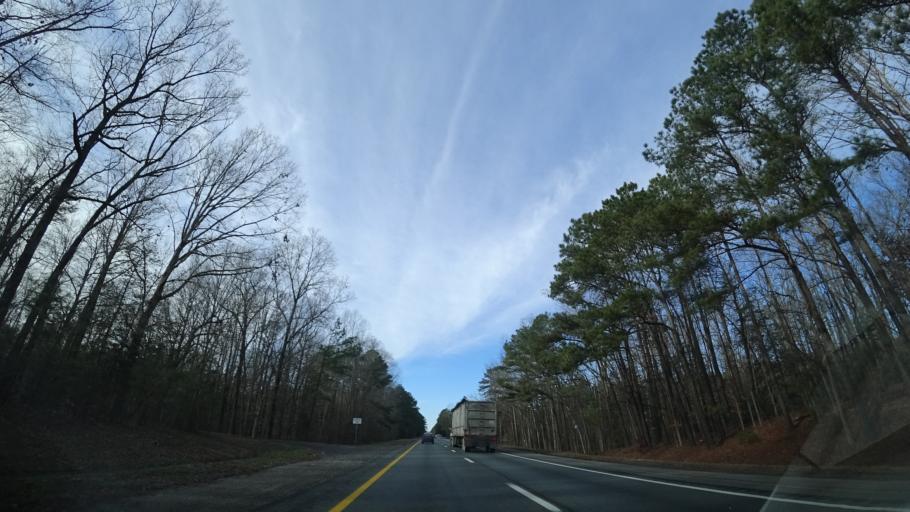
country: US
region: Virginia
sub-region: New Kent County
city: New Kent
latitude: 37.4800
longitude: -76.9293
